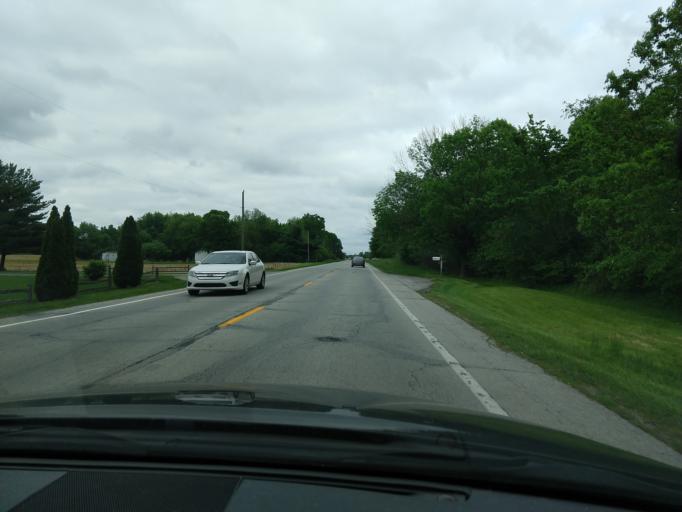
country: US
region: Indiana
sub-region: Madison County
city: Lapel
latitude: 40.0592
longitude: -85.8934
